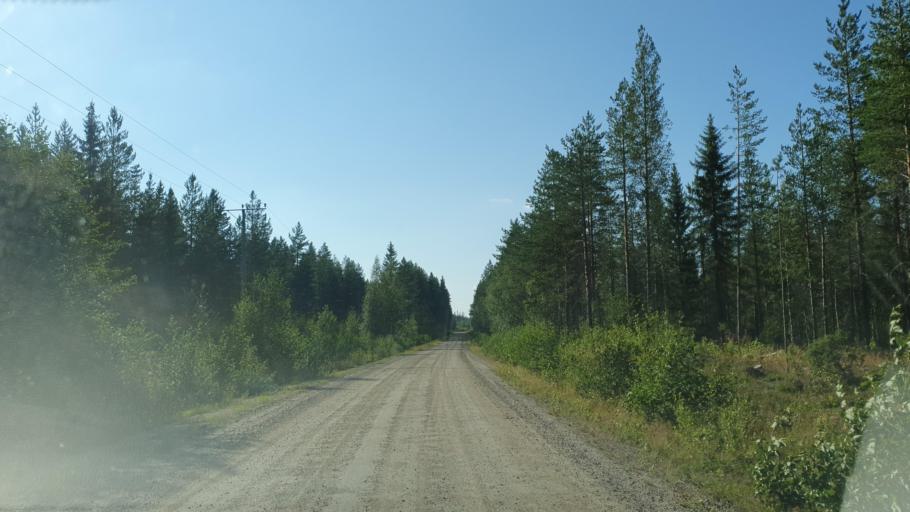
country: FI
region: Kainuu
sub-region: Kehys-Kainuu
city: Kuhmo
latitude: 64.0289
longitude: 29.6999
